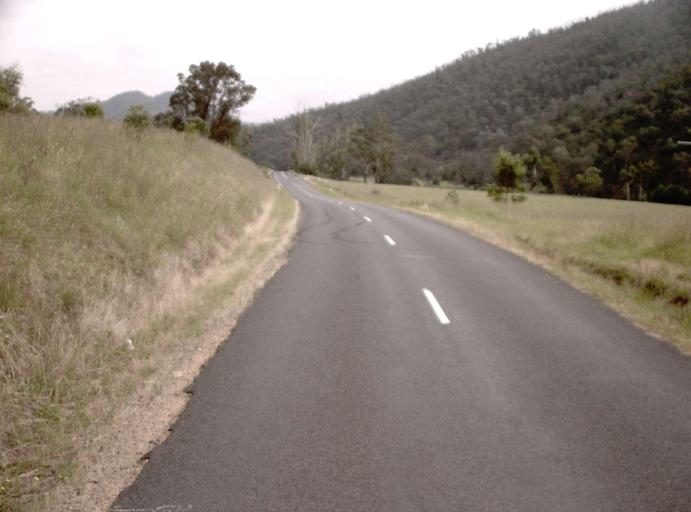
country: AU
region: Victoria
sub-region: Wellington
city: Heyfield
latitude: -37.7661
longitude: 146.6682
